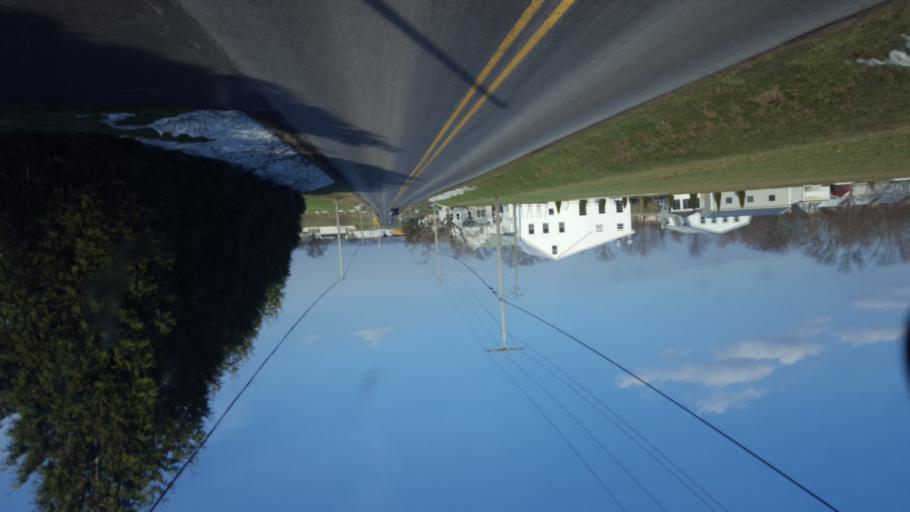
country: US
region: Pennsylvania
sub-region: Lancaster County
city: Brownstown
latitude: 40.0758
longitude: -76.1924
